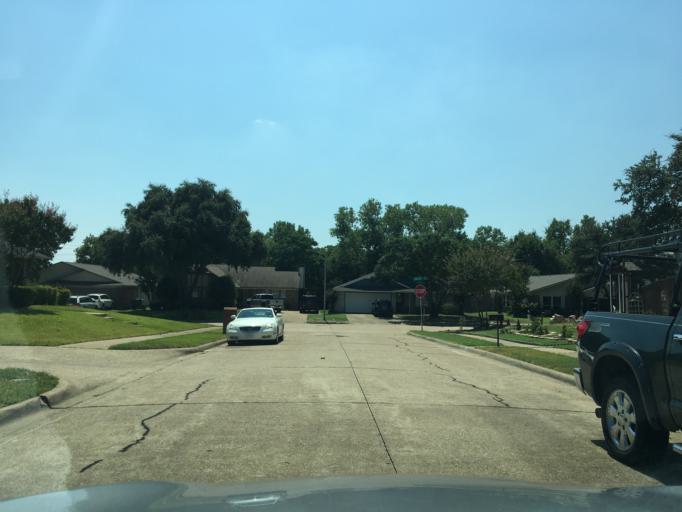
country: US
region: Texas
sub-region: Dallas County
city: Garland
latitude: 32.9533
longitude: -96.6659
